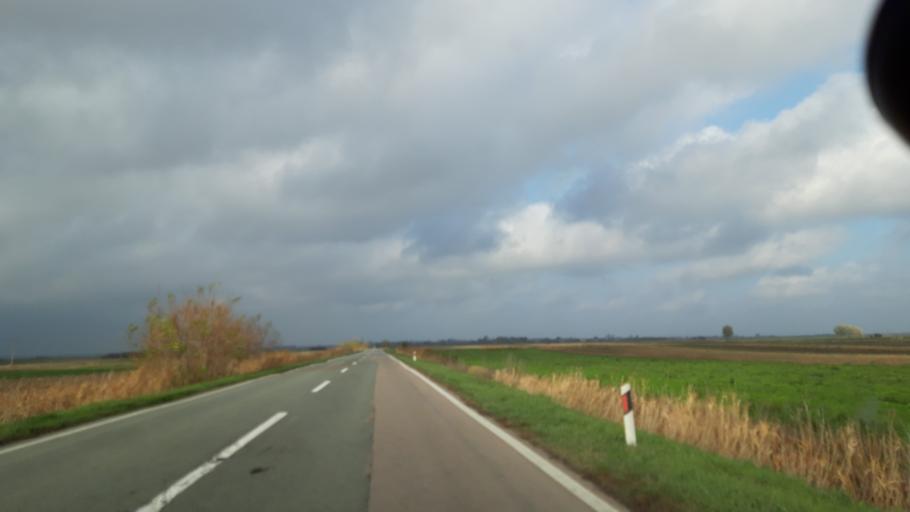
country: RS
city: Ostojicevo
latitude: 45.9098
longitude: 20.1528
